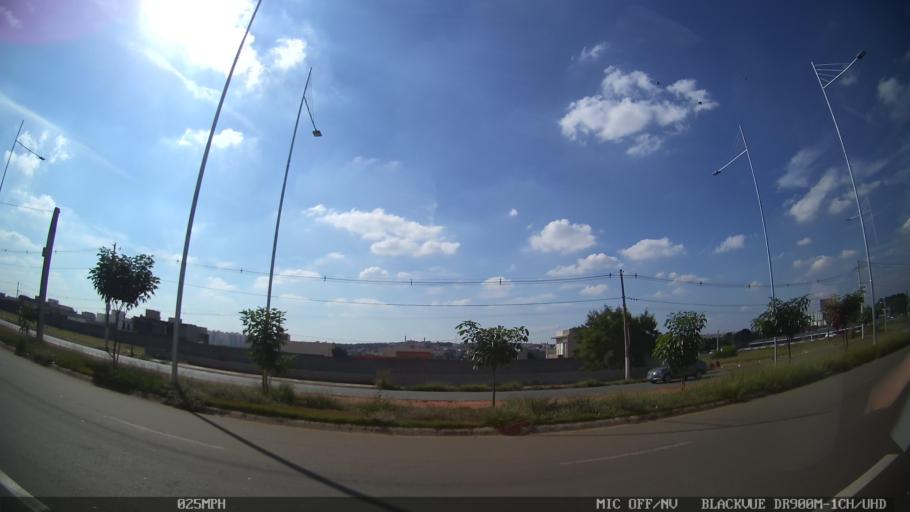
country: BR
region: Sao Paulo
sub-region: Hortolandia
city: Hortolandia
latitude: -22.8671
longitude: -47.2271
